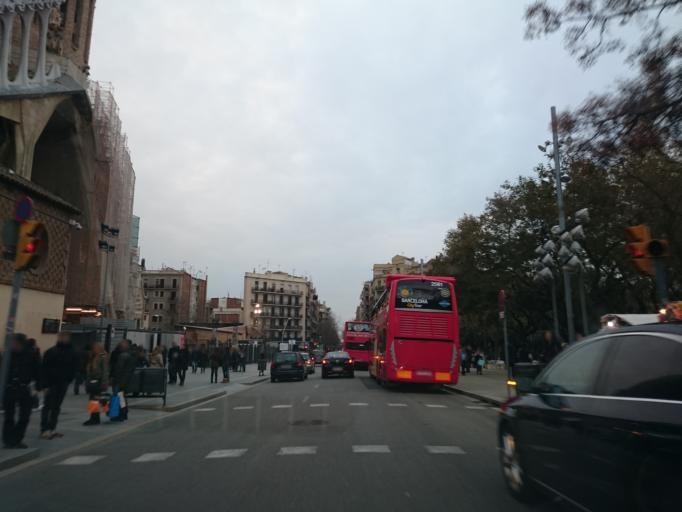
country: ES
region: Catalonia
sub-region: Provincia de Barcelona
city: Horta-Guinardo
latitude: 41.4034
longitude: 2.1734
